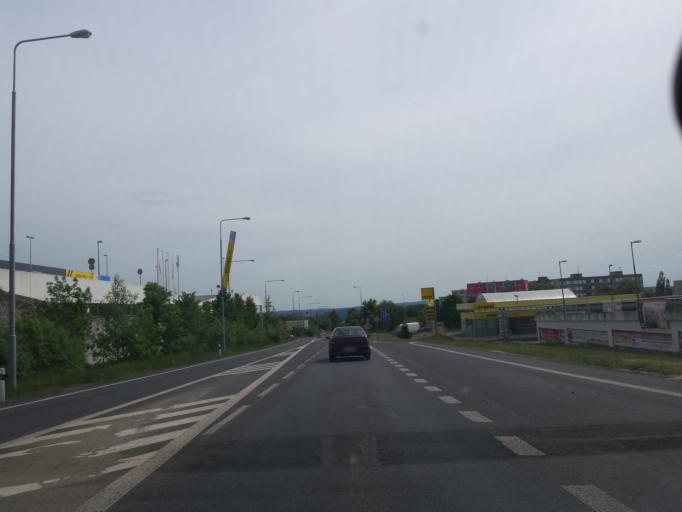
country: CZ
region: Liberecky
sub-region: Okres Ceska Lipa
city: Ceska Lipa
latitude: 50.6999
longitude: 14.5422
